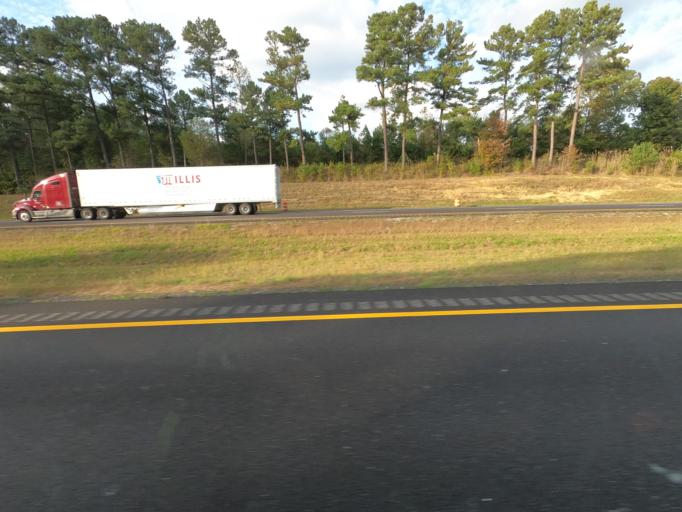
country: US
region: Tennessee
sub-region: Decatur County
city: Parsons
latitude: 35.8197
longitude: -88.1623
